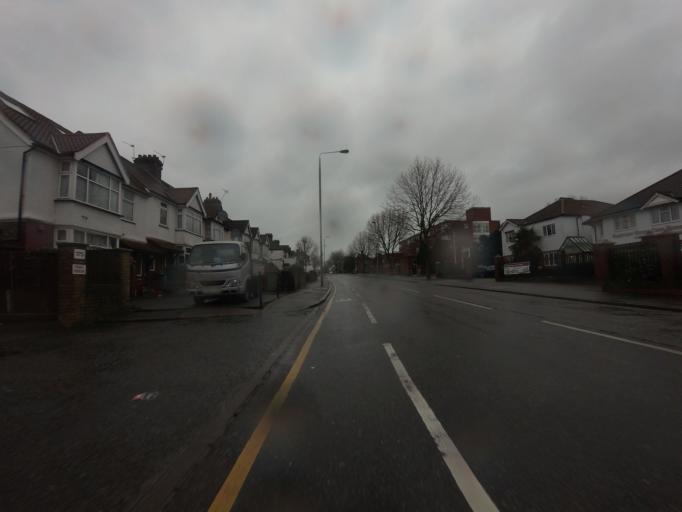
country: GB
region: England
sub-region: Greater London
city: Walthamstow
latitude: 51.6140
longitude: -0.0175
